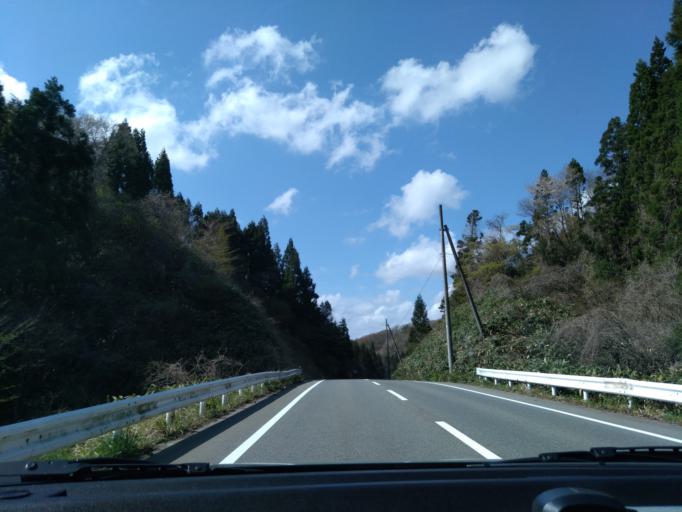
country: JP
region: Akita
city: Akita
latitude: 39.6958
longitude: 140.2214
